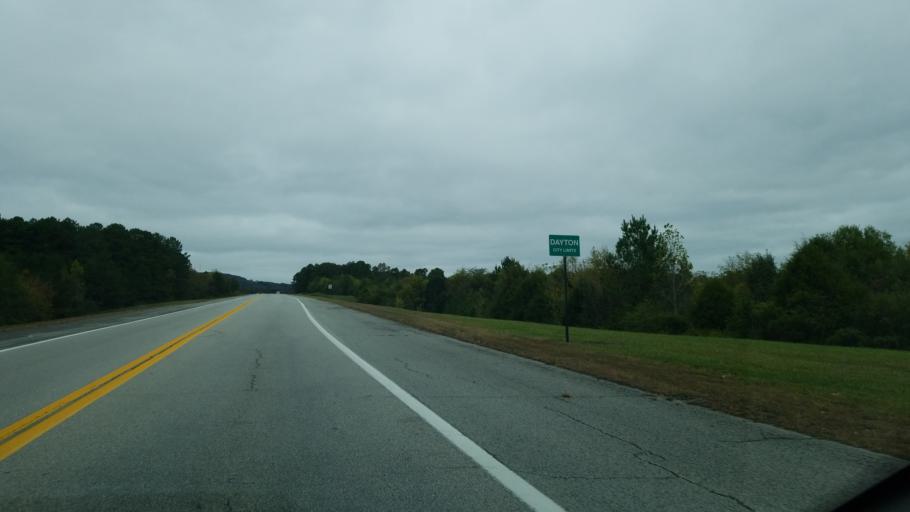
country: US
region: Tennessee
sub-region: Rhea County
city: Dayton
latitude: 35.4608
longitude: -85.0143
